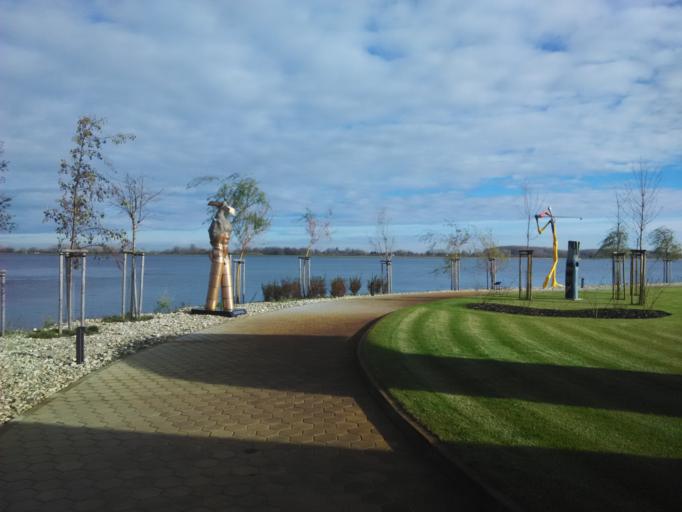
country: HU
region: Gyor-Moson-Sopron
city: Rajka
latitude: 48.0358
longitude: 17.2307
